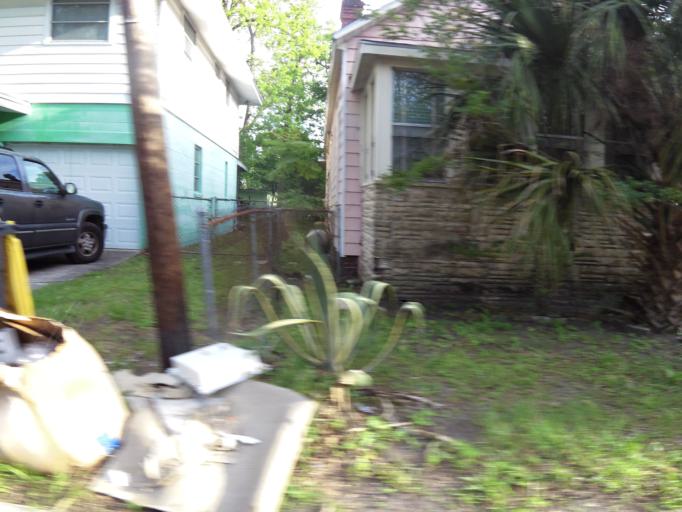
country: US
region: Florida
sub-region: Duval County
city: Jacksonville
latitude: 30.3541
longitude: -81.6659
